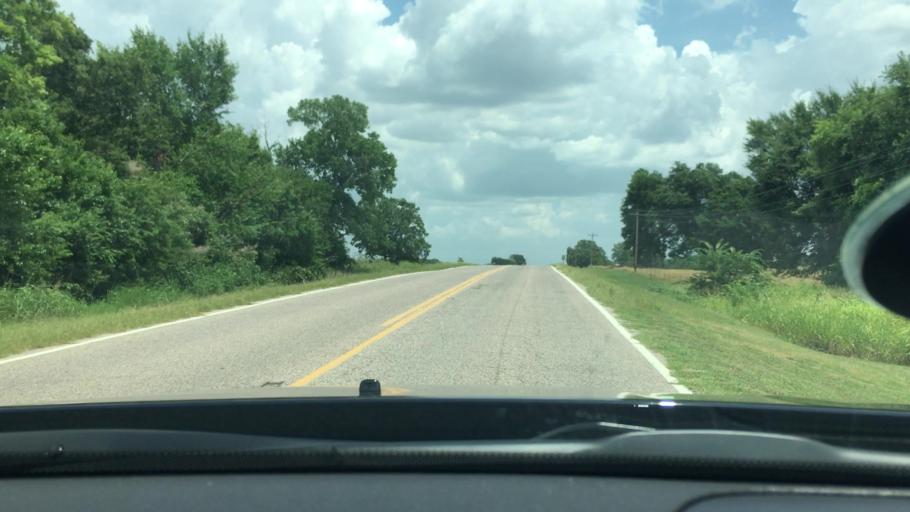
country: US
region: Texas
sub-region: Grayson County
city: Sherwood Shores
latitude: 33.9839
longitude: -96.9338
